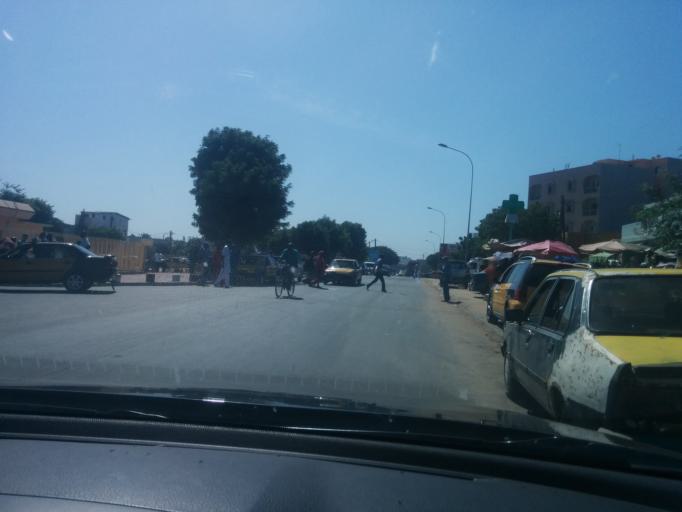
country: SN
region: Dakar
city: Grand Dakar
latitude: 14.7321
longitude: -17.4463
